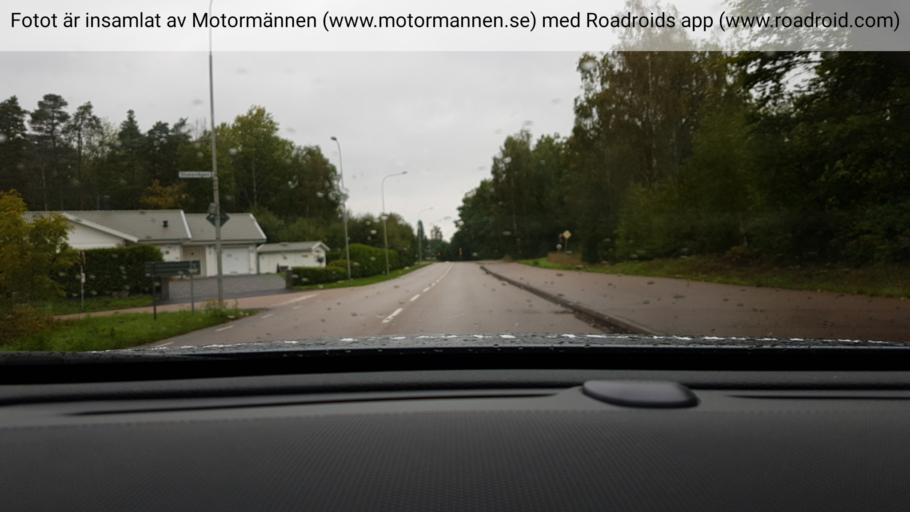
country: SE
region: Vaestra Goetaland
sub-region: Vanersborgs Kommun
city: Vargon
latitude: 58.3443
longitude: 12.3551
